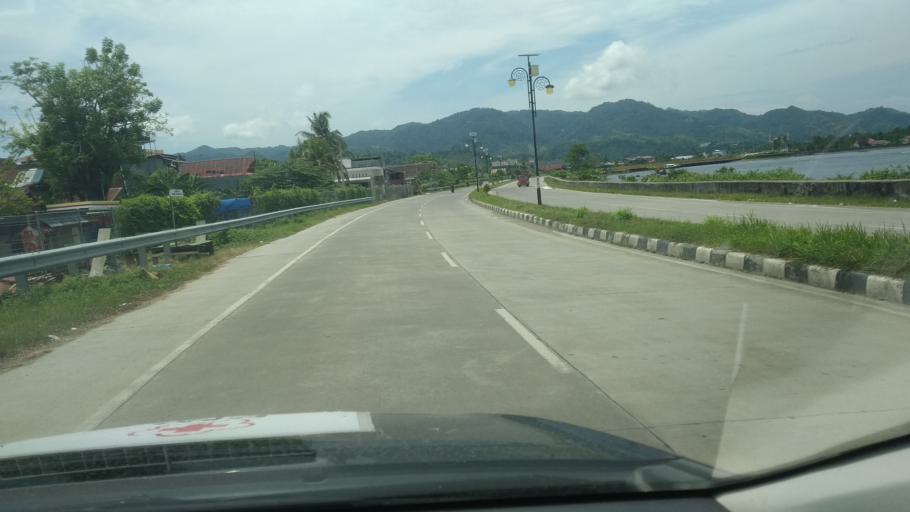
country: ID
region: Sulawesi Barat
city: Mamuju
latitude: -2.6808
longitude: 118.8717
